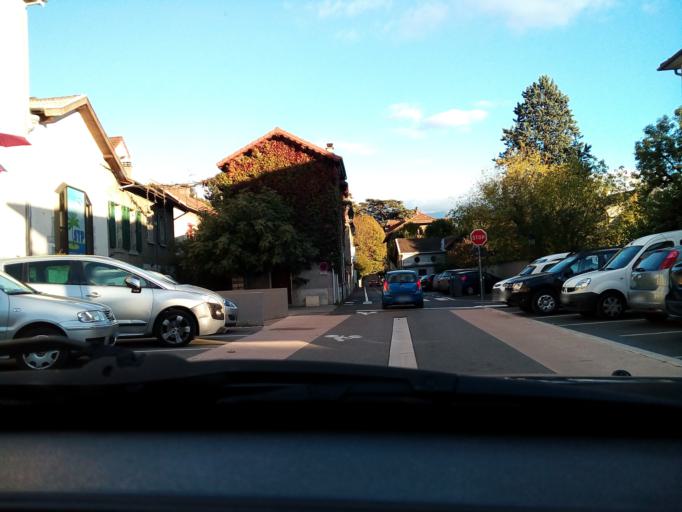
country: FR
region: Rhone-Alpes
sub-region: Departement de l'Isere
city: La Tronche
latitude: 45.2067
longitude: 5.7459
